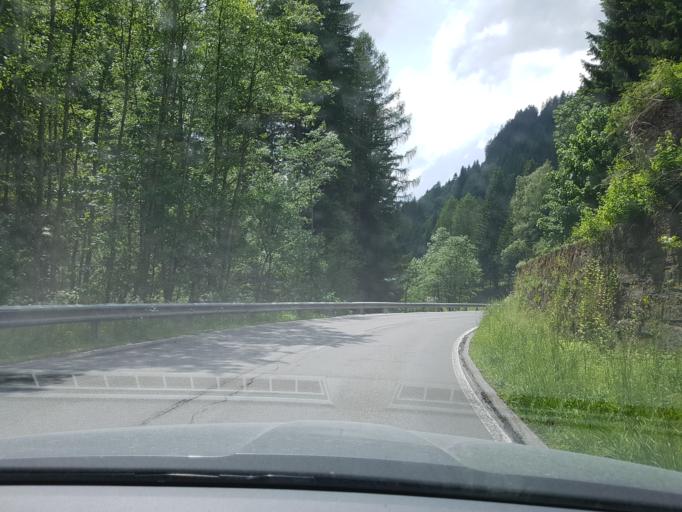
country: AT
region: Carinthia
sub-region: Politischer Bezirk Villach Land
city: Feld am See
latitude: 46.8043
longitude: 13.7590
